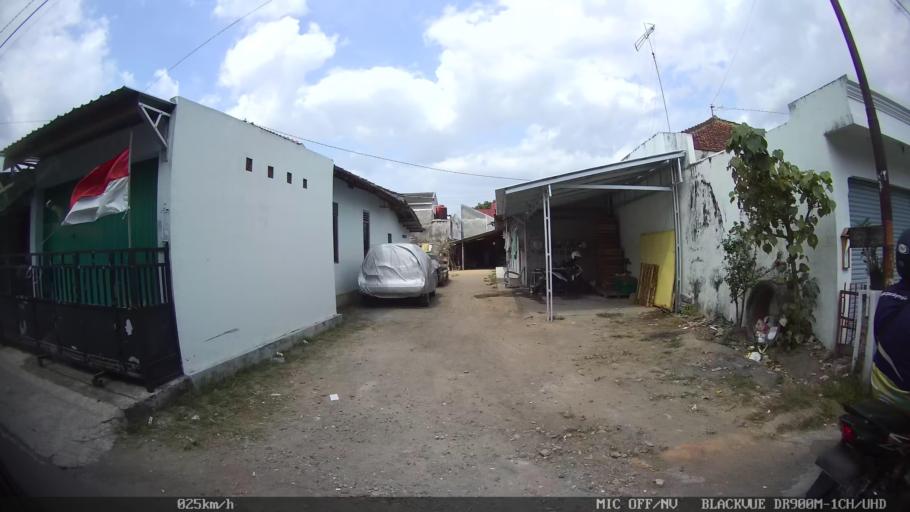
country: ID
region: Daerah Istimewa Yogyakarta
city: Gamping Lor
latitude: -7.8048
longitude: 110.3376
